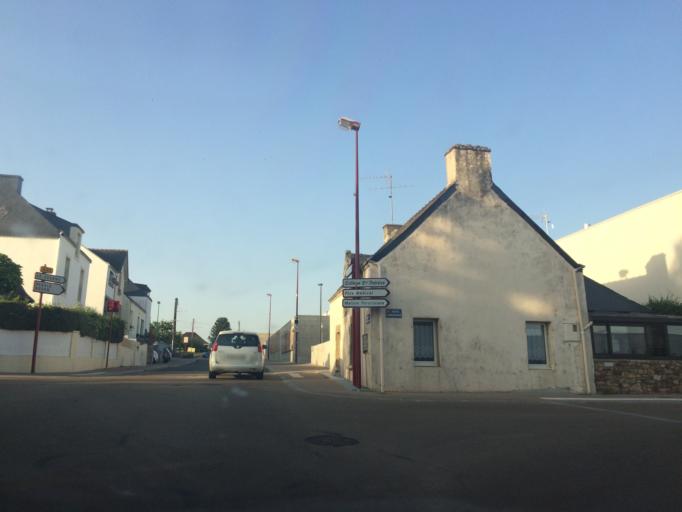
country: FR
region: Brittany
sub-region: Departement du Morbihan
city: Muzillac
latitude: 47.5551
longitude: -2.4804
